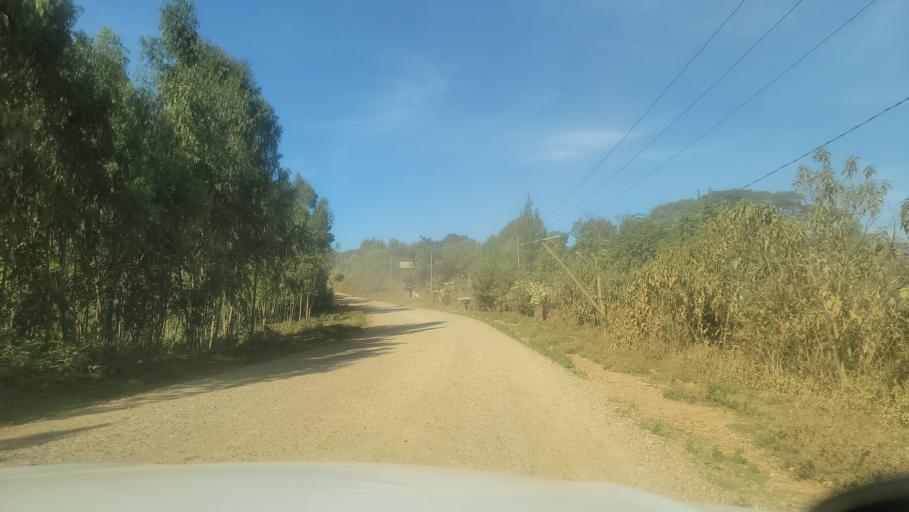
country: ET
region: Oromiya
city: Agaro
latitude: 7.8144
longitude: 36.5136
